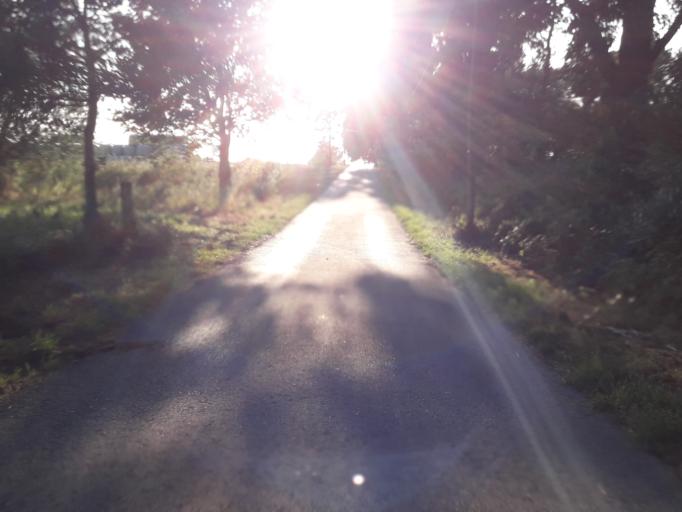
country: DE
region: North Rhine-Westphalia
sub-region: Regierungsbezirk Detmold
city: Paderborn
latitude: 51.7130
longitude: 8.6822
